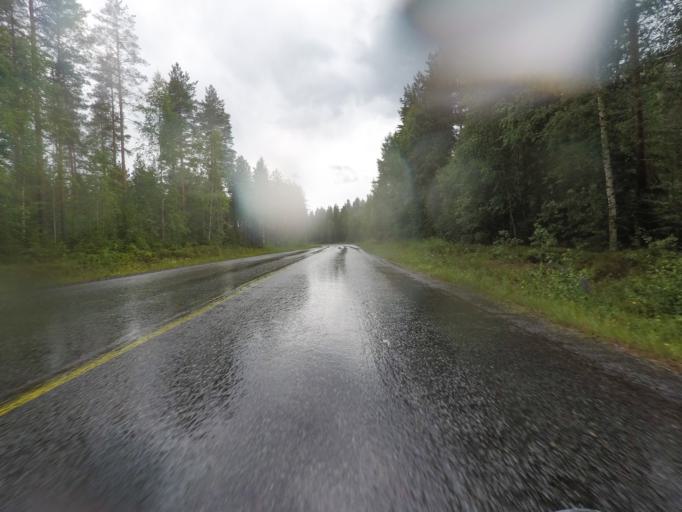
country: FI
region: Central Finland
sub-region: Jyvaeskylae
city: Toivakka
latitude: 62.1773
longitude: 26.1774
